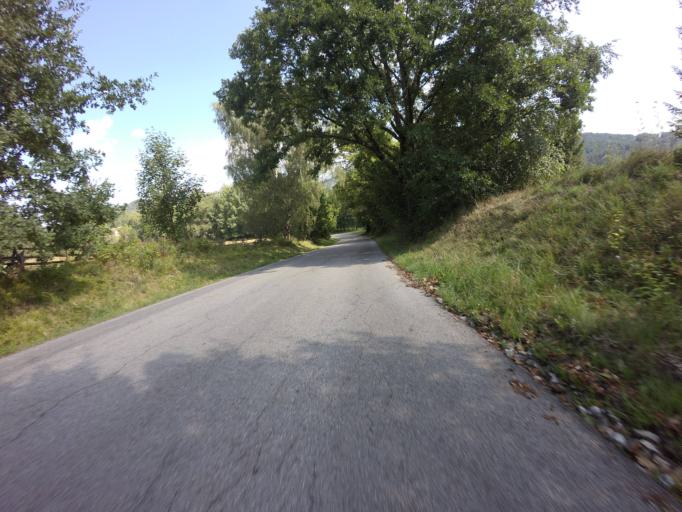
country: CZ
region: Jihocesky
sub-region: Okres Cesky Krumlov
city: Vyssi Brod
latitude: 48.6479
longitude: 14.3586
